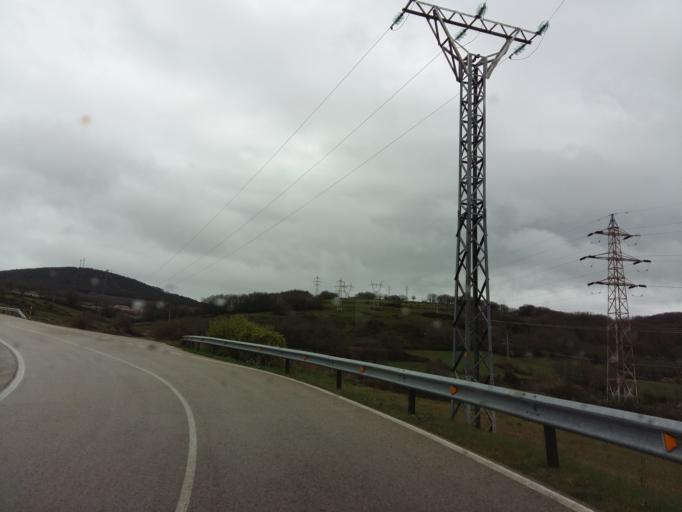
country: ES
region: Cantabria
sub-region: Provincia de Cantabria
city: Mataporquera
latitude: 42.8871
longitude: -4.1579
